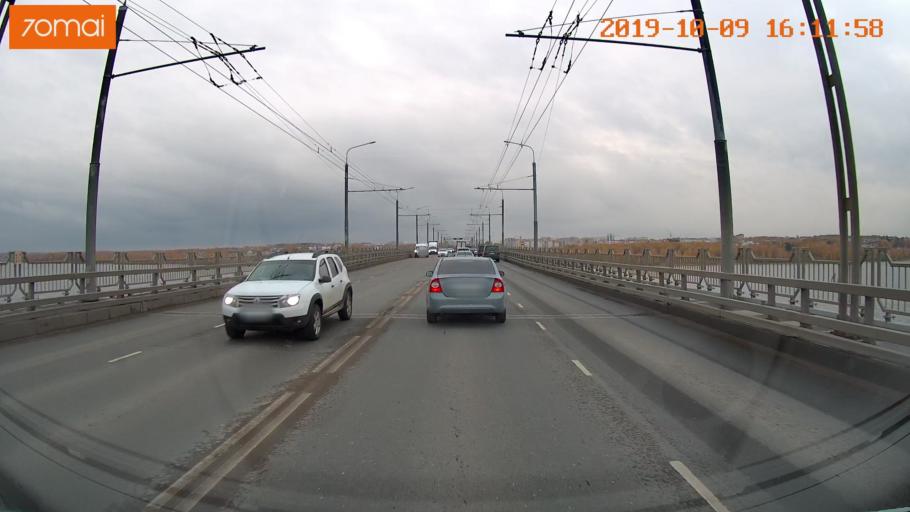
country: RU
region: Kostroma
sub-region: Kostromskoy Rayon
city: Kostroma
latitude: 57.7540
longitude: 40.9410
